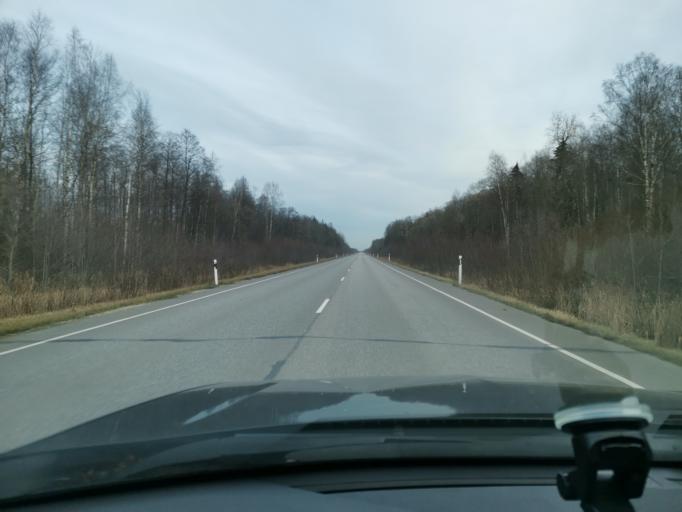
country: EE
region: Ida-Virumaa
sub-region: Narva-Joesuu linn
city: Narva-Joesuu
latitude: 59.3298
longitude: 27.9424
